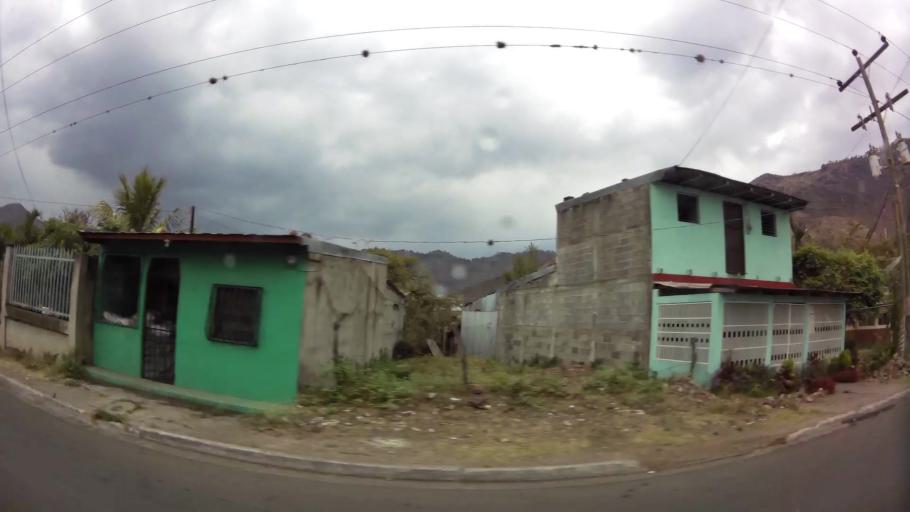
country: NI
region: Jinotega
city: Jinotega
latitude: 13.0913
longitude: -85.9957
